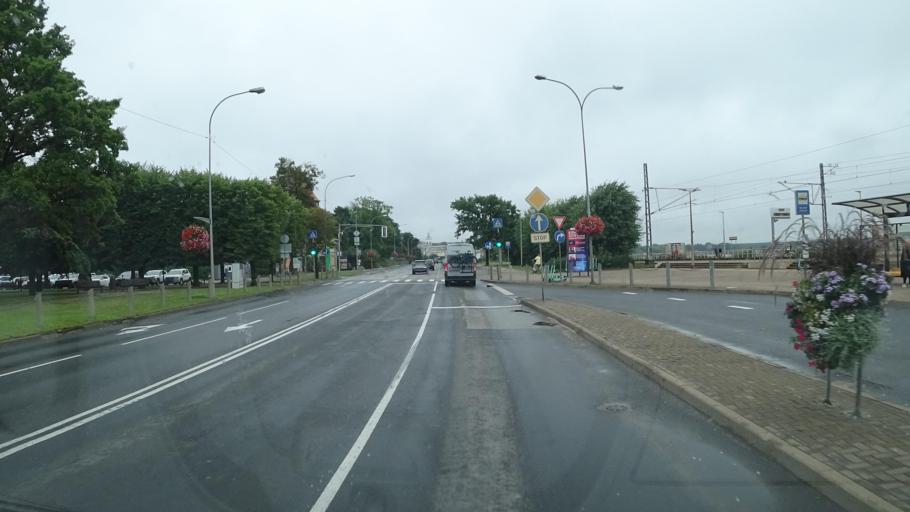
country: LV
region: Jurmala
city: Jurmala
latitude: 56.9707
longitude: 23.7962
